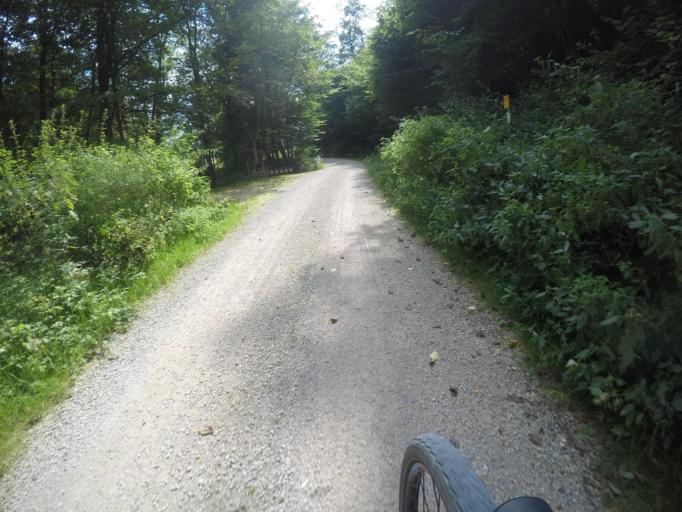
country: DE
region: Baden-Wuerttemberg
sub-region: Tuebingen Region
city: Bad Urach
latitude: 48.4749
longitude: 9.4066
